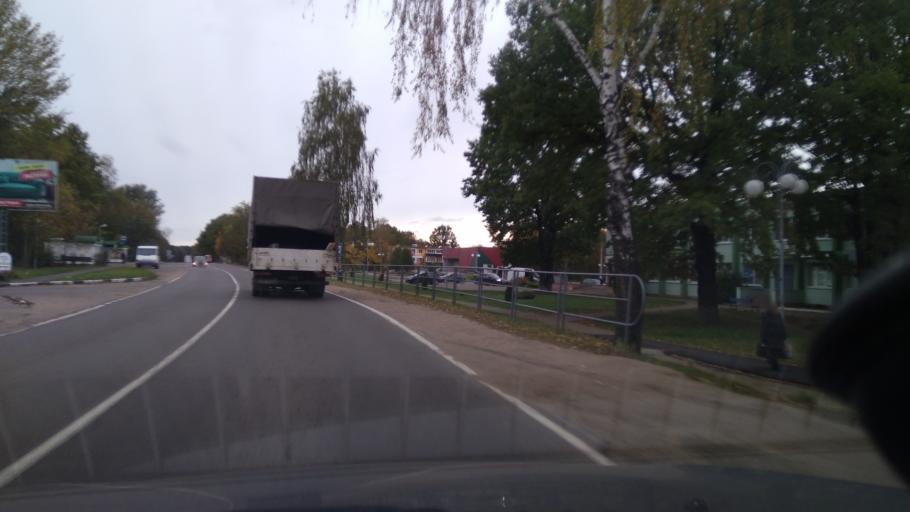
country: BY
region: Minsk
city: Svislach
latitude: 53.6466
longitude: 27.9177
